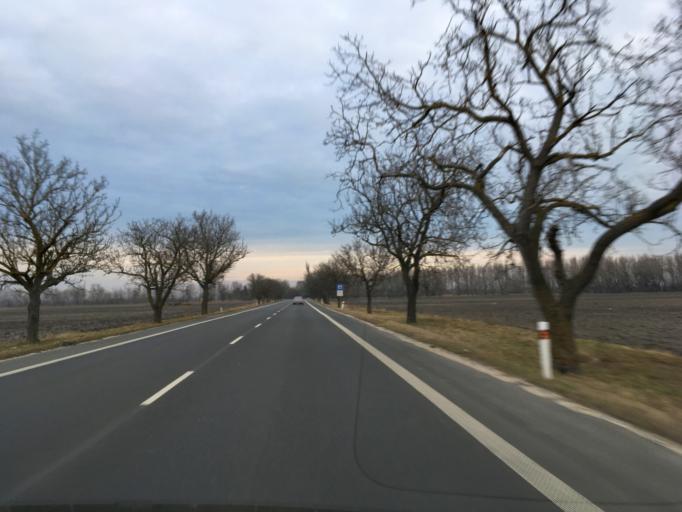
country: SK
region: Trnavsky
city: Dunajska Streda
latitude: 47.9525
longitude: 17.7053
